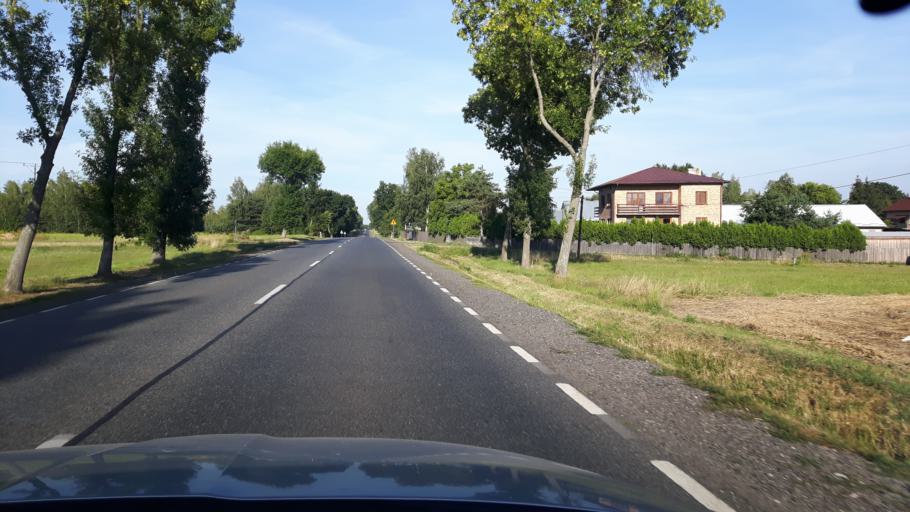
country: PL
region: Masovian Voivodeship
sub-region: Powiat nowodworski
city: Brody-Parcele
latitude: 52.4891
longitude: 20.8177
